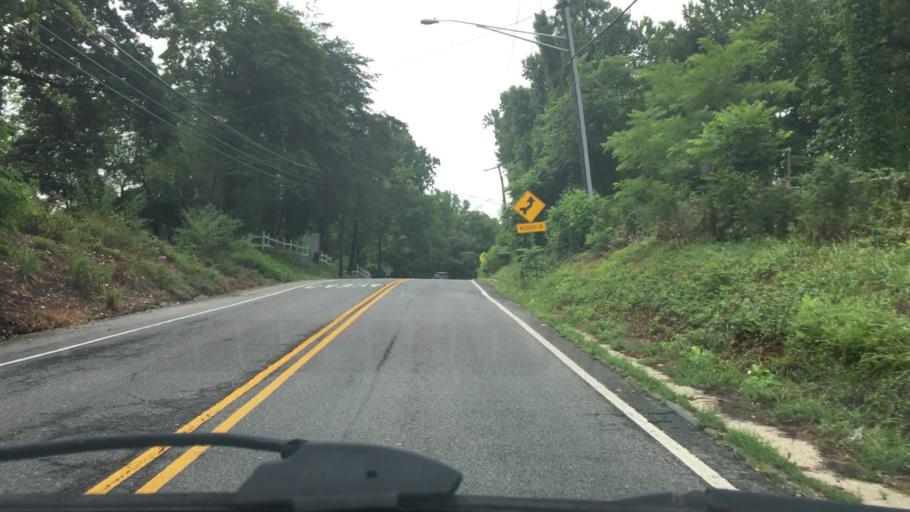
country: US
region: Maryland
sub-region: Prince George's County
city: Glenn Dale
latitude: 38.9809
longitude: -76.7716
